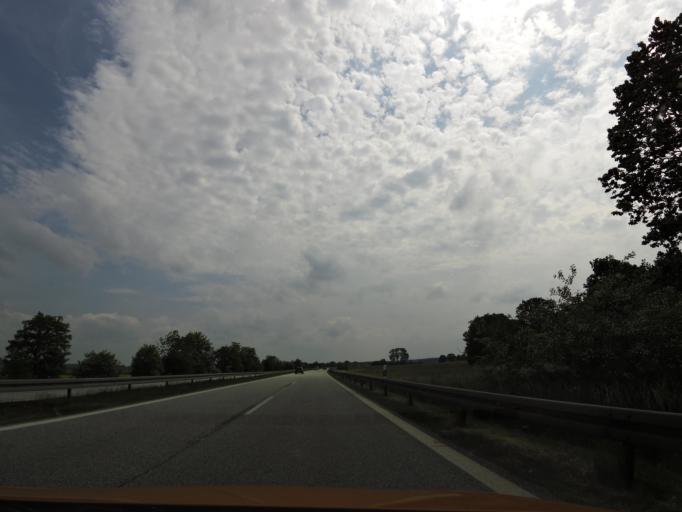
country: DE
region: Mecklenburg-Vorpommern
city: Mirow
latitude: 53.4532
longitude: 11.4997
